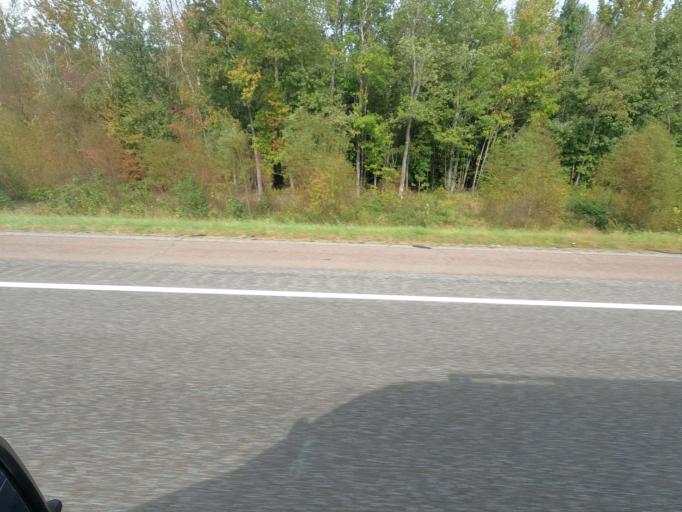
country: US
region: Tennessee
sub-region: Henderson County
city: Lexington
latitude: 35.7483
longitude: -88.5509
